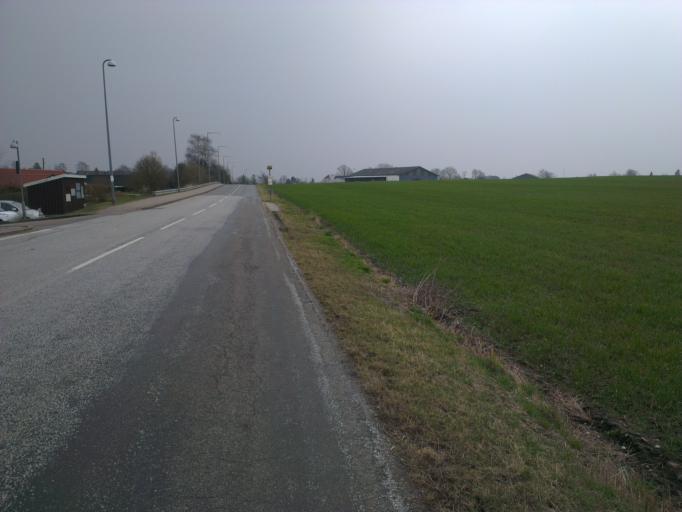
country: DK
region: Capital Region
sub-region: Egedal Kommune
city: Olstykke
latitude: 55.8018
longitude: 12.1125
